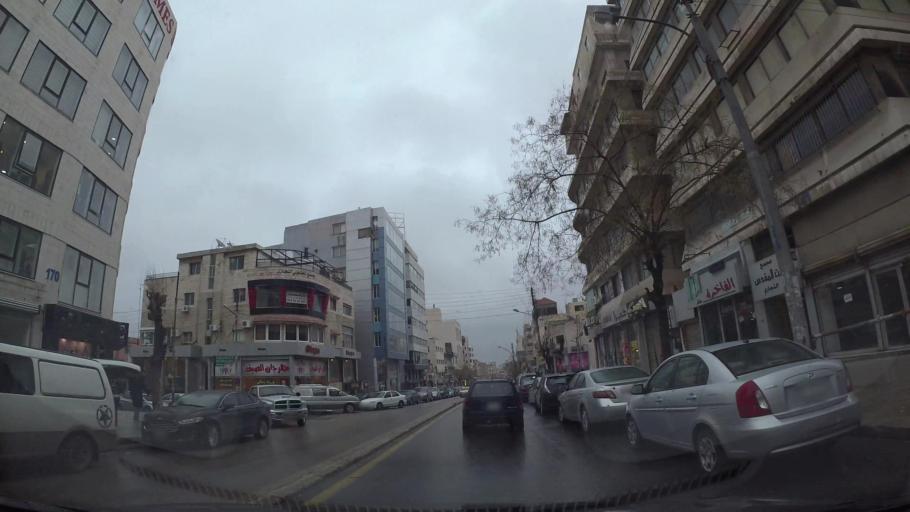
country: JO
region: Amman
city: Amman
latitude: 31.9663
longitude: 35.9196
